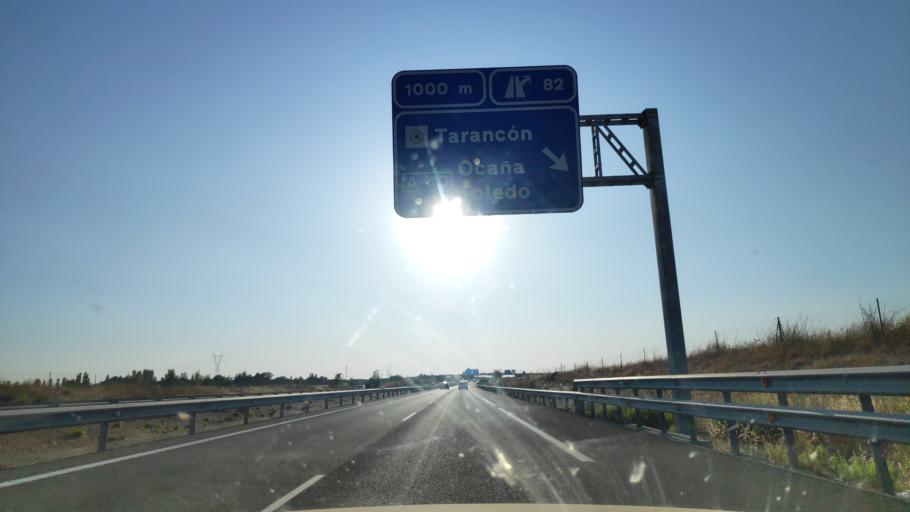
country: ES
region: Castille-La Mancha
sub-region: Provincia de Cuenca
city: Tarancon
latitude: 39.9931
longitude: -2.9990
